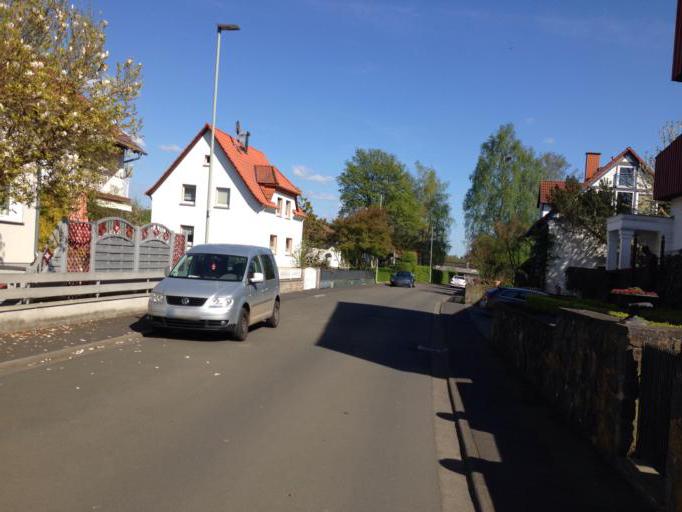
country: DE
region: Hesse
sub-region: Regierungsbezirk Giessen
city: Grunberg
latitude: 50.5576
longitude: 8.9081
